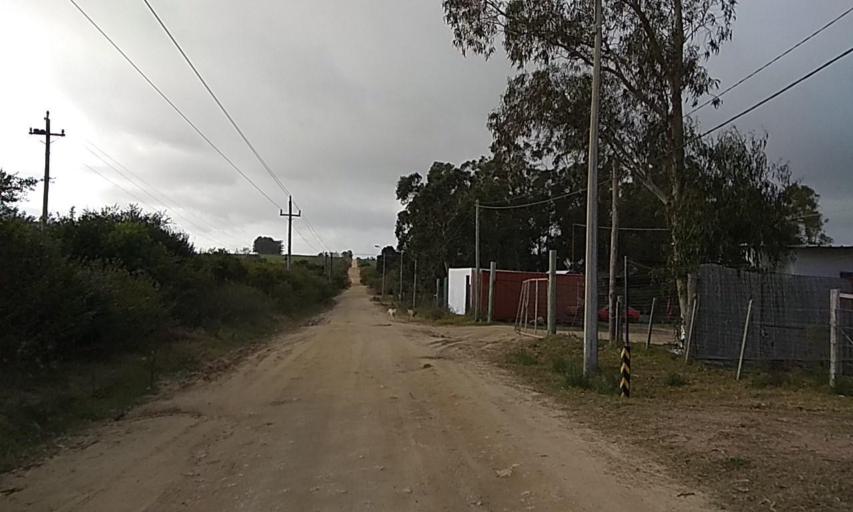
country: UY
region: Florida
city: Florida
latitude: -34.0587
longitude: -56.2172
